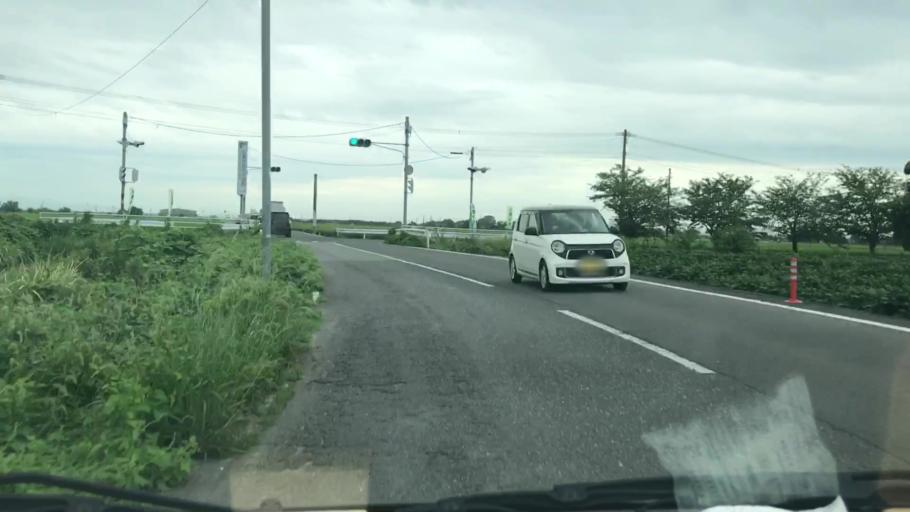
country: JP
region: Saga Prefecture
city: Saga-shi
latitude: 33.2276
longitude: 130.2740
